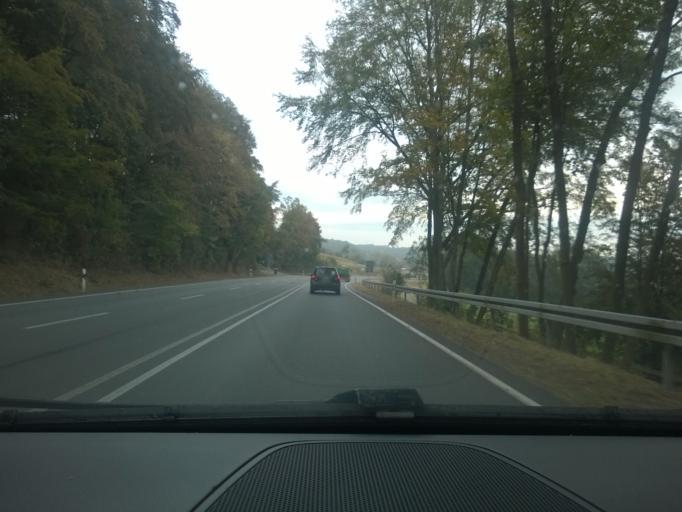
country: DE
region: North Rhine-Westphalia
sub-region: Regierungsbezirk Munster
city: Billerbeck
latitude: 51.9320
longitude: 7.2857
